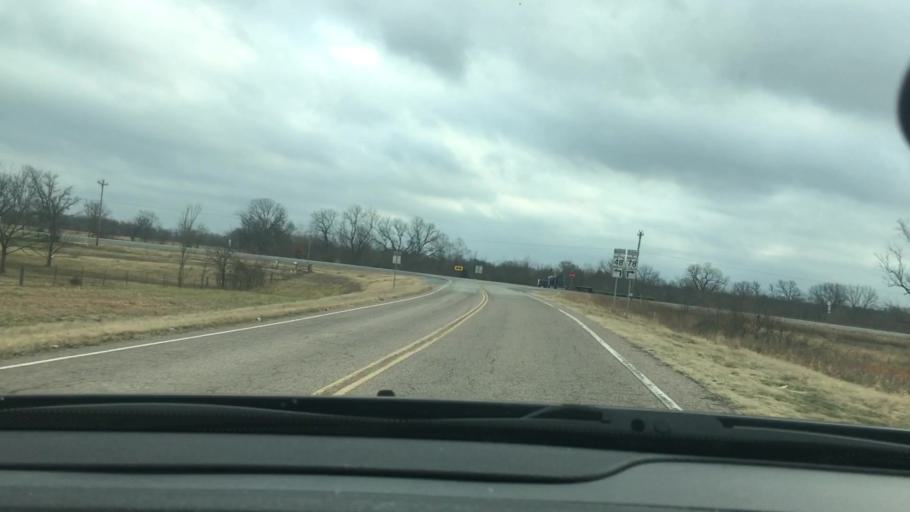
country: US
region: Oklahoma
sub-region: Bryan County
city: Durant
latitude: 34.0809
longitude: -96.3747
